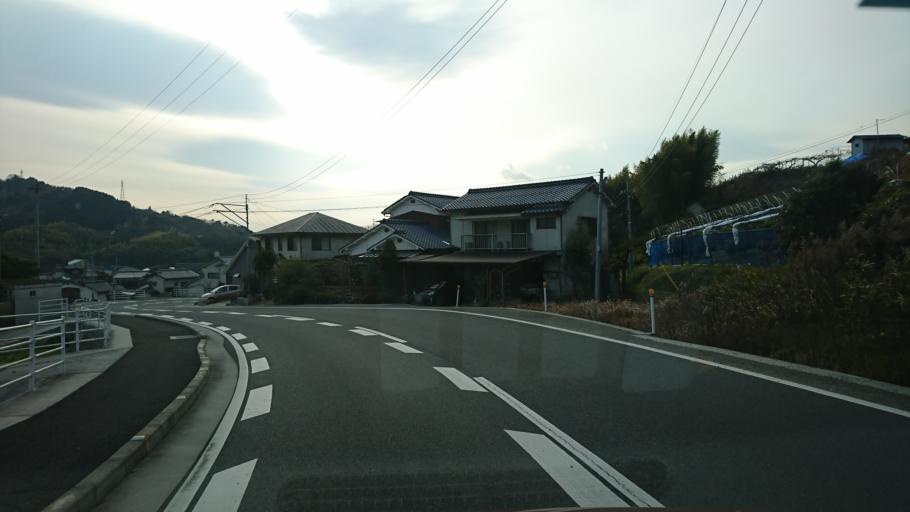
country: JP
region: Ehime
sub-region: Shikoku-chuo Shi
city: Matsuyama
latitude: 33.8803
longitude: 132.8017
